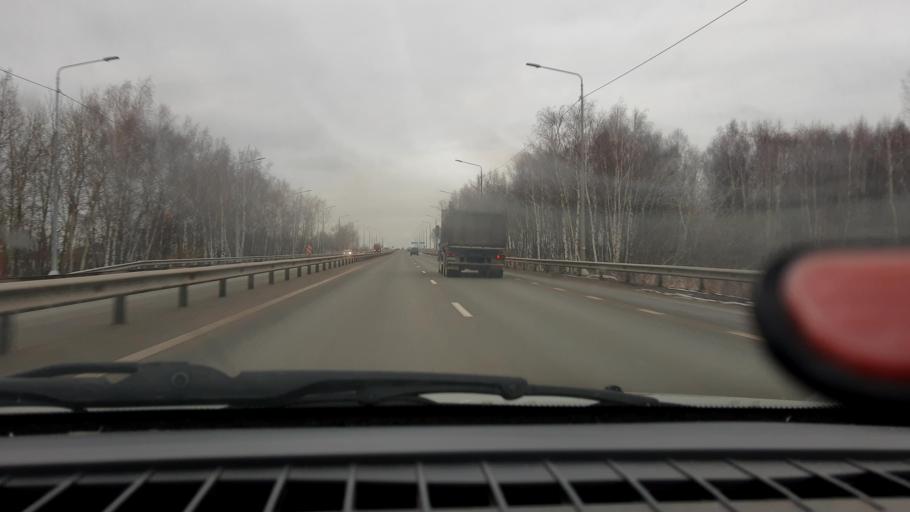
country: RU
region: Nizjnij Novgorod
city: Burevestnik
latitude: 56.1060
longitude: 43.9179
